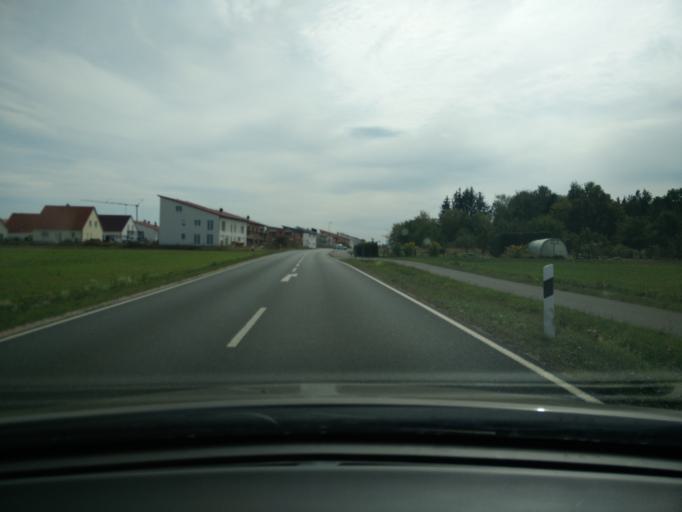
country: DE
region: Bavaria
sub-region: Regierungsbezirk Mittelfranken
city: Seukendorf
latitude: 49.4931
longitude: 10.8764
